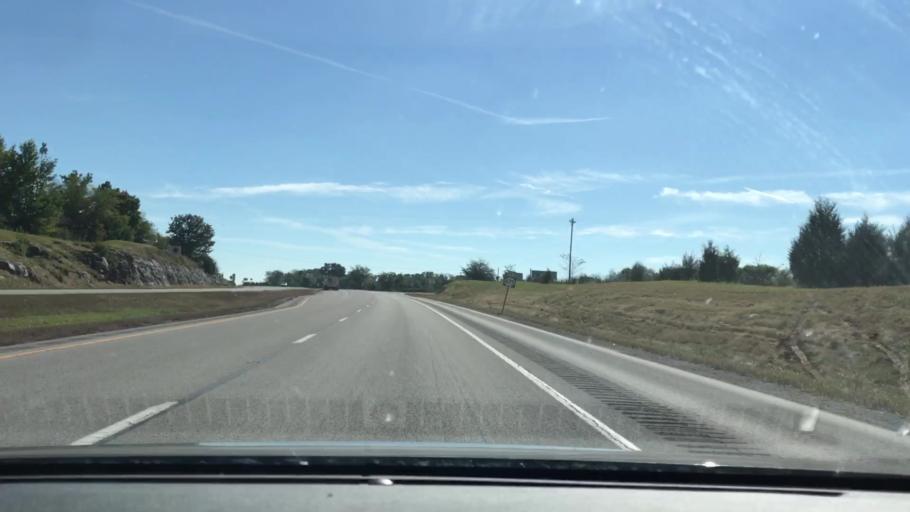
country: US
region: Kentucky
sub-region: Todd County
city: Elkton
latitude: 36.8280
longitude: -87.2230
